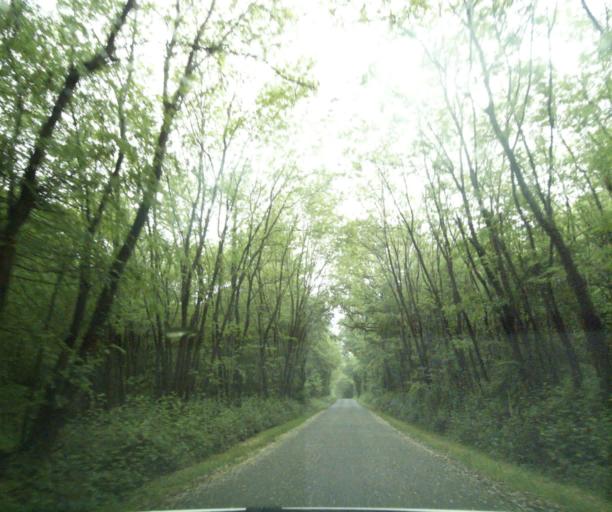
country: FR
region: Bourgogne
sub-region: Departement de Saone-et-Loire
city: Paray-le-Monial
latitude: 46.4189
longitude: 4.1952
